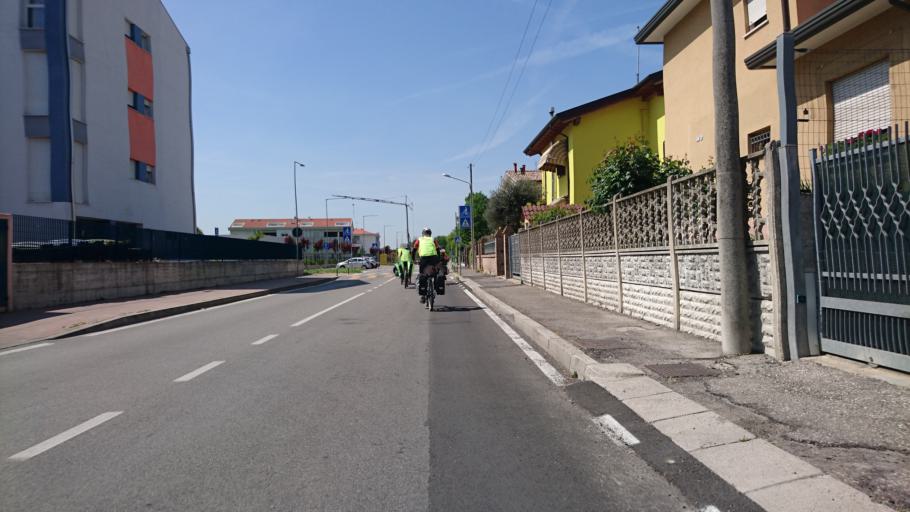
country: IT
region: Veneto
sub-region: Provincia di Padova
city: Vigodarzere
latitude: 45.4489
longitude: 11.8783
